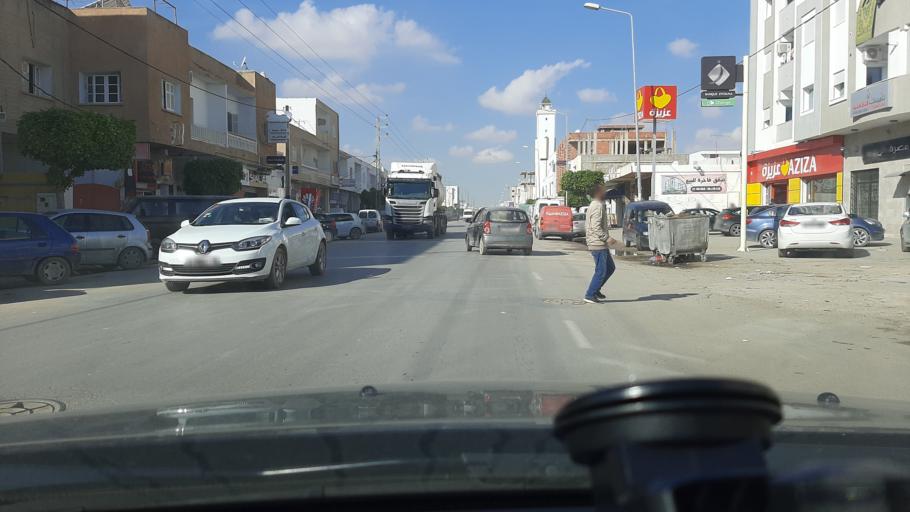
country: TN
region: Safaqis
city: Sfax
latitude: 34.7922
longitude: 10.7162
